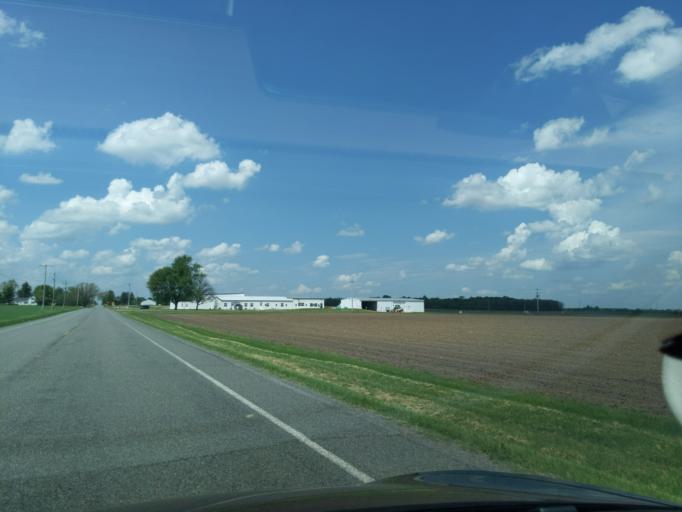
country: US
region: Michigan
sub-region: Ingham County
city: Mason
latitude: 42.6221
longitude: -84.4330
